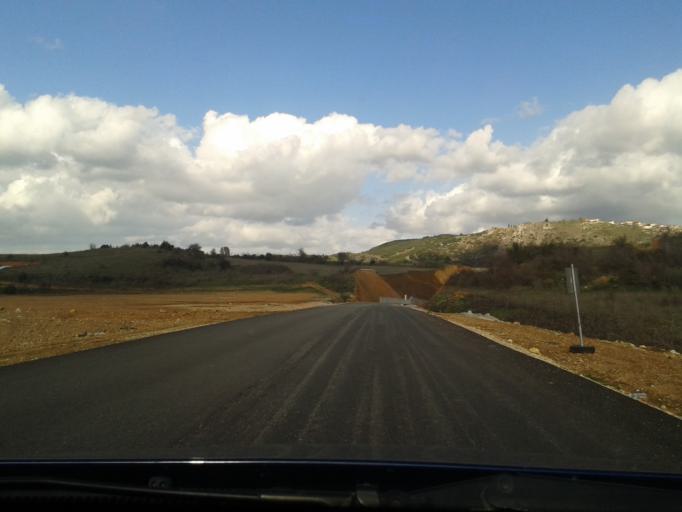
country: GR
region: West Greece
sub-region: Nomos Aitolias kai Akarnanias
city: Fitiai
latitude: 38.6847
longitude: 21.1688
